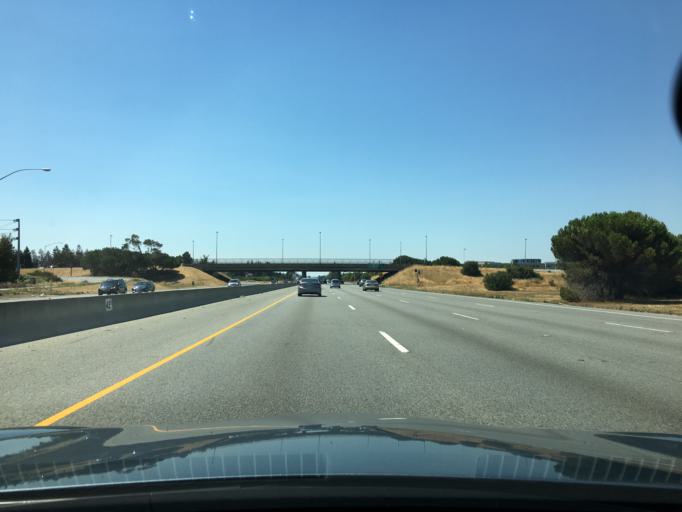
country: US
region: California
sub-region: Santa Clara County
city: Santa Clara
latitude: 37.3849
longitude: -121.9739
